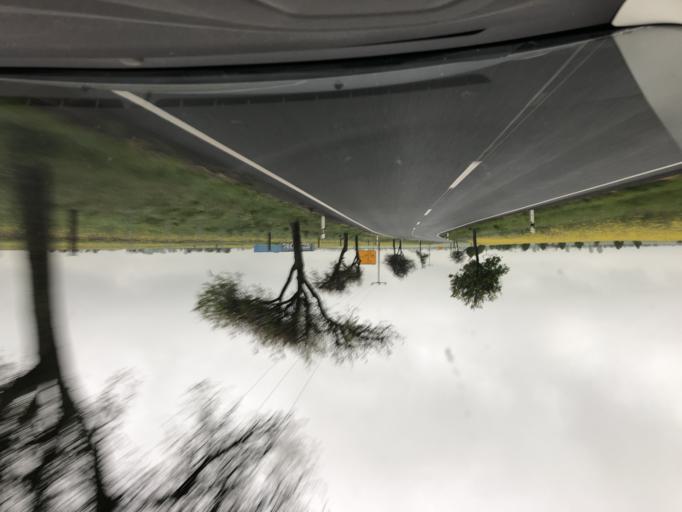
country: DE
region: Saxony
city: Krostitz
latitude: 51.4554
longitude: 12.4939
